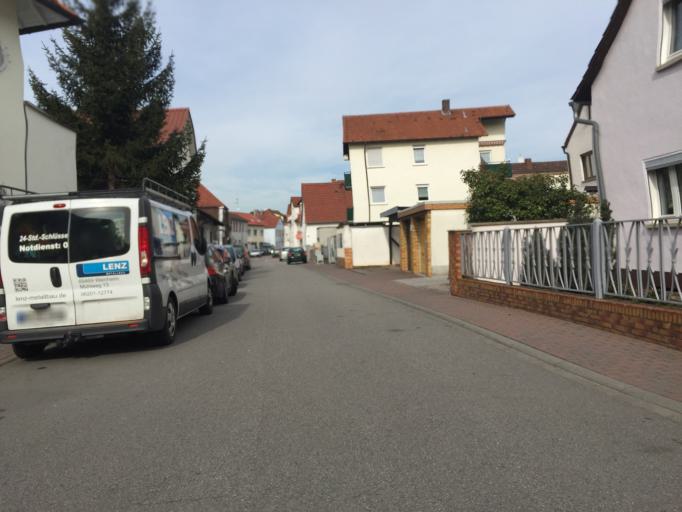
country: DE
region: Hesse
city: Viernheim
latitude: 49.5395
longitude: 8.5838
